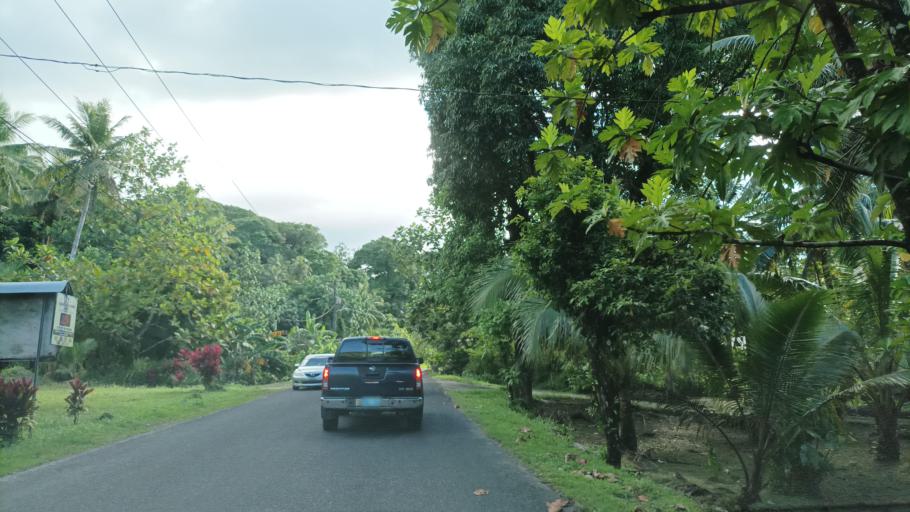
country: FM
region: Pohnpei
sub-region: Kolonia Municipality
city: Kolonia
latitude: 6.9546
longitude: 158.2456
